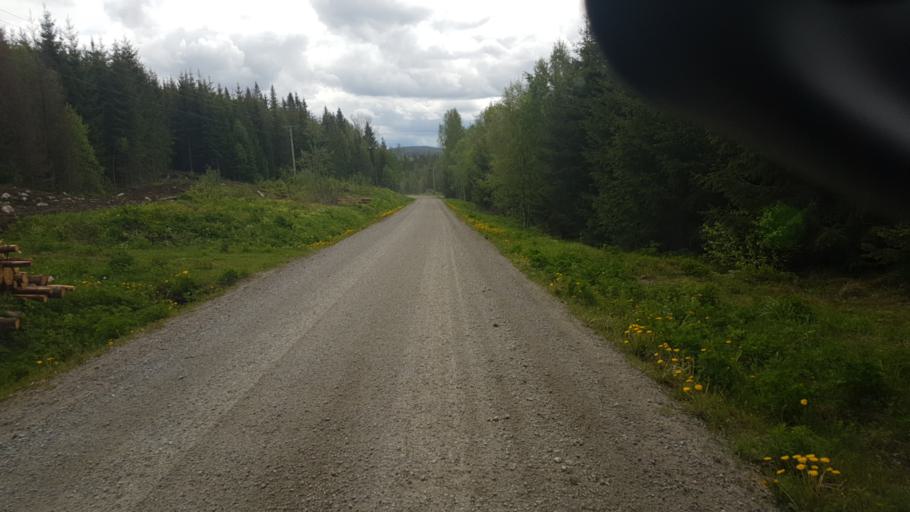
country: SE
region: Vaermland
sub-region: Arvika Kommun
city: Arvika
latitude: 59.8435
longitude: 12.7291
